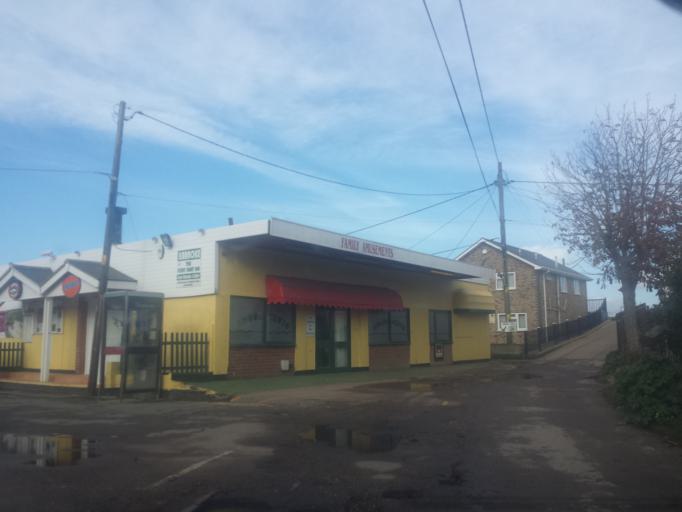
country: GB
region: England
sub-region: Essex
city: Brightlingsea
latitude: 51.8013
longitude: 1.0198
